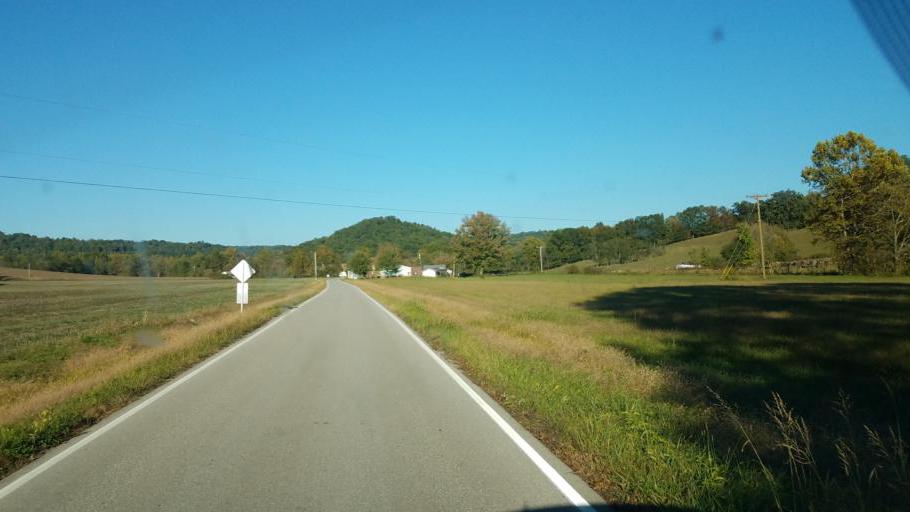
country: US
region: Ohio
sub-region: Adams County
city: Manchester
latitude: 38.5062
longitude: -83.5457
